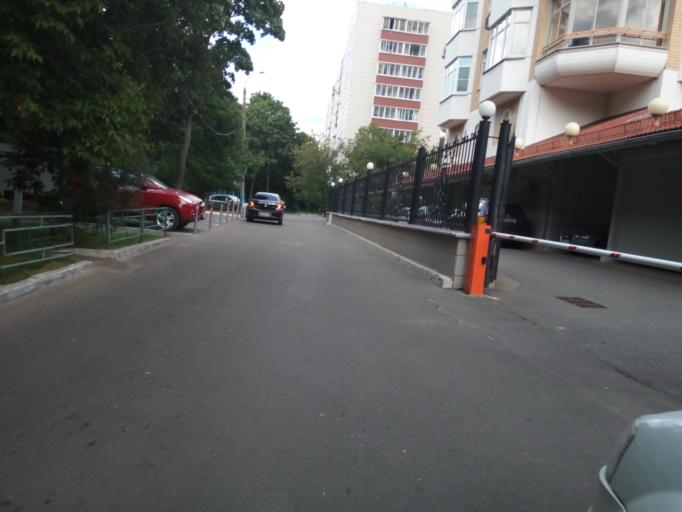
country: RU
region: Moscow
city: Sokol
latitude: 55.7795
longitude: 37.5190
